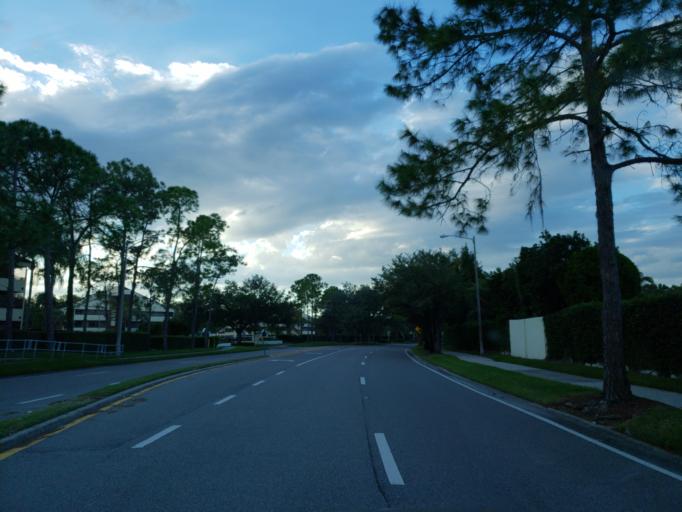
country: US
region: Florida
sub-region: Hillsborough County
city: Carrollwood Village
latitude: 28.0714
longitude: -82.5198
